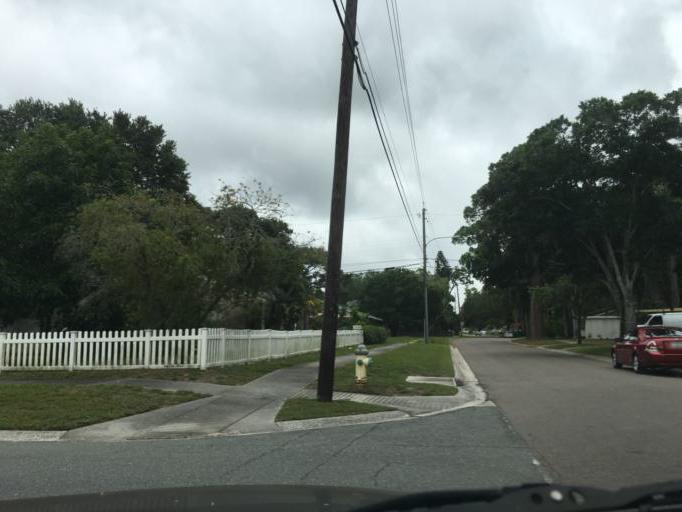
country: US
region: Florida
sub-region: Pinellas County
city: Lealman
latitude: 27.8149
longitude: -82.6447
